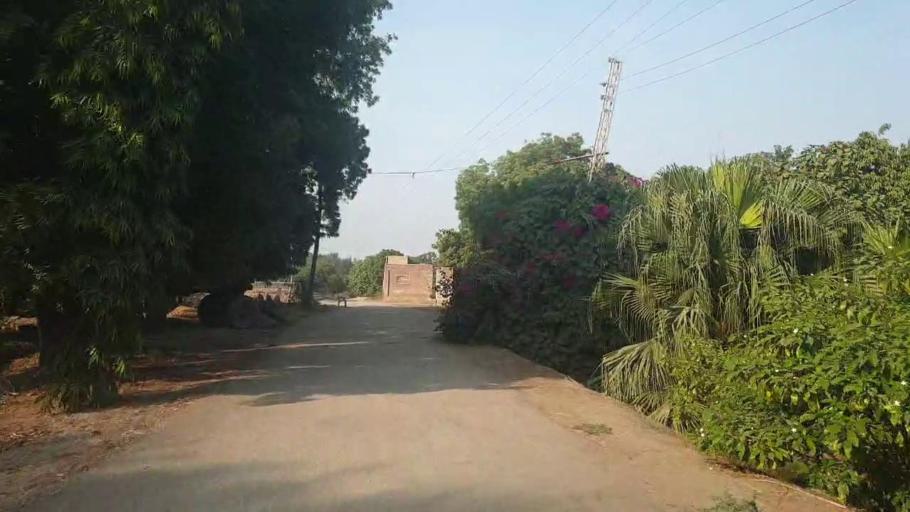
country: PK
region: Sindh
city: Tando Jam
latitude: 25.4299
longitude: 68.4649
